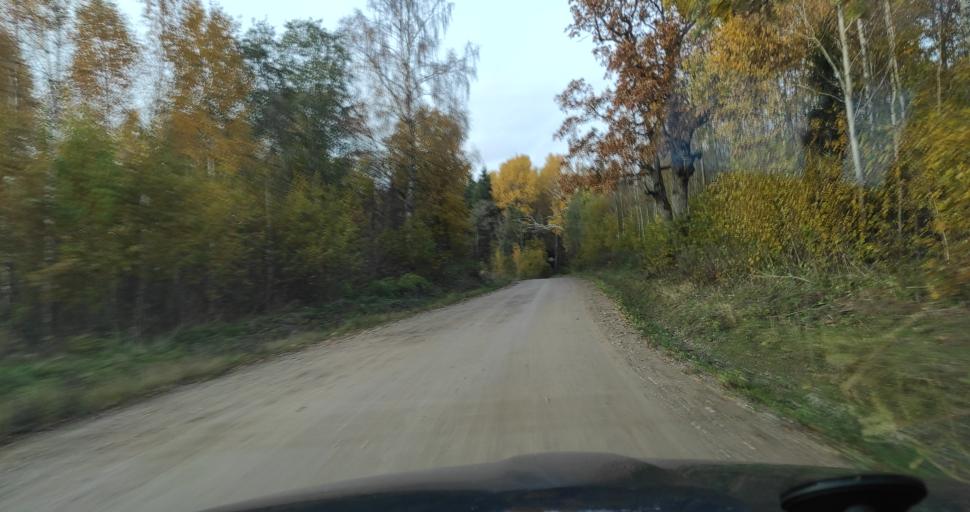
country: LV
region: Vainode
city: Vainode
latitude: 56.6284
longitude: 21.8170
